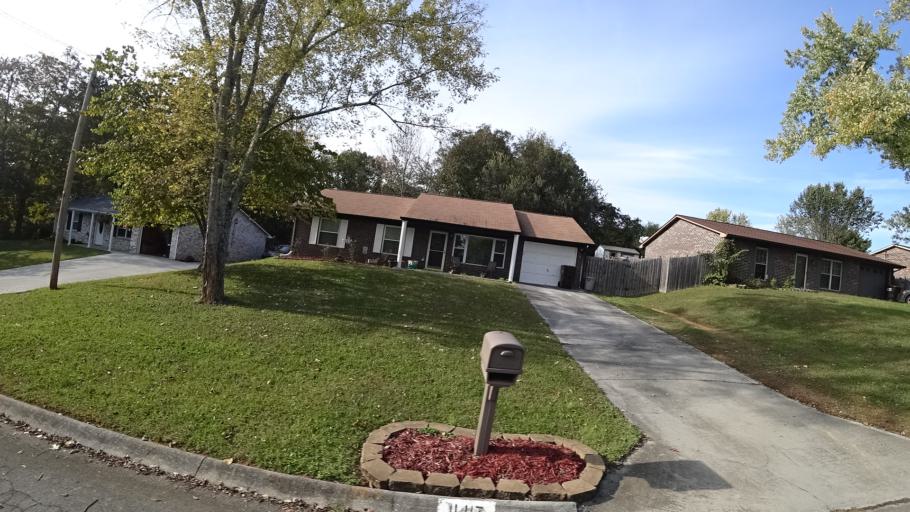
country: US
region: Tennessee
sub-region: Knox County
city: Farragut
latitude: 35.9100
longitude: -84.1650
